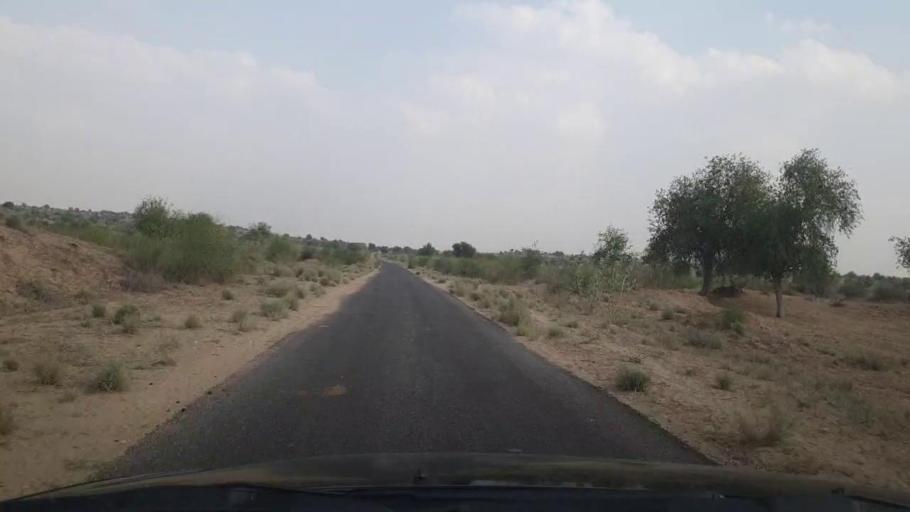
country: PK
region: Sindh
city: Islamkot
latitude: 25.0118
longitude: 70.6373
